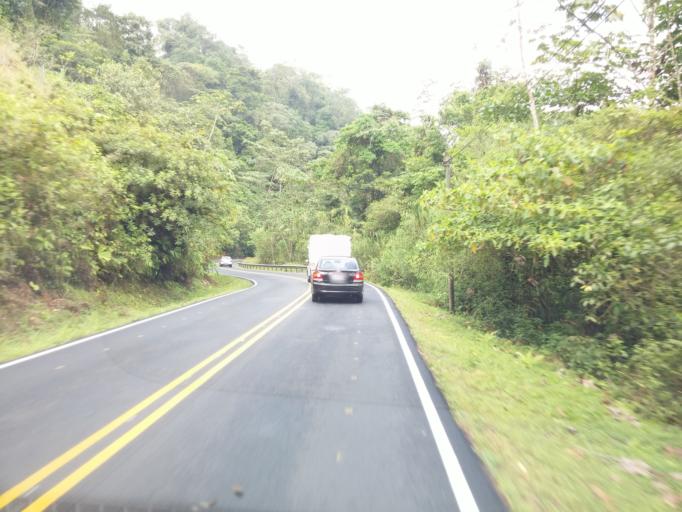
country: CR
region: Alajuela
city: San Ramon
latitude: 10.2171
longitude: -84.5421
